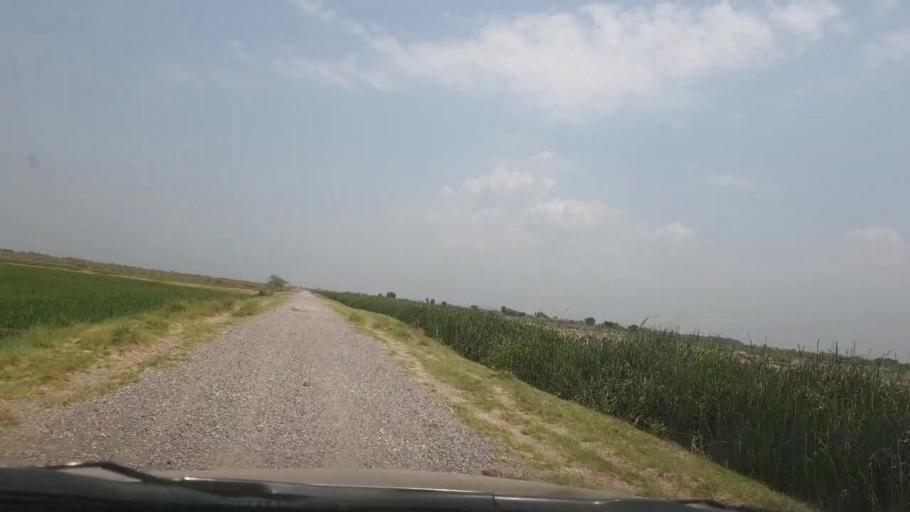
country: PK
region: Sindh
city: Naudero
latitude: 27.7208
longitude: 68.3108
